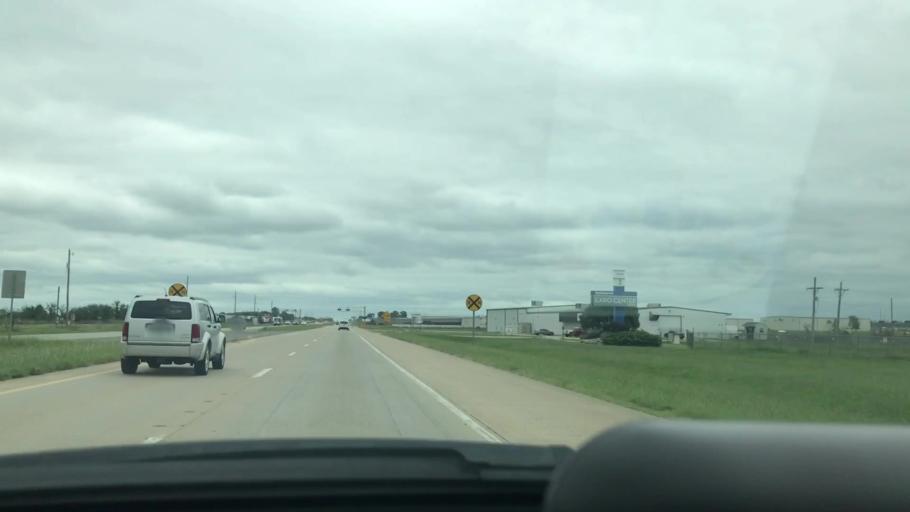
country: US
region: Oklahoma
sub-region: Mayes County
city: Chouteau
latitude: 36.2342
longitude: -95.3388
